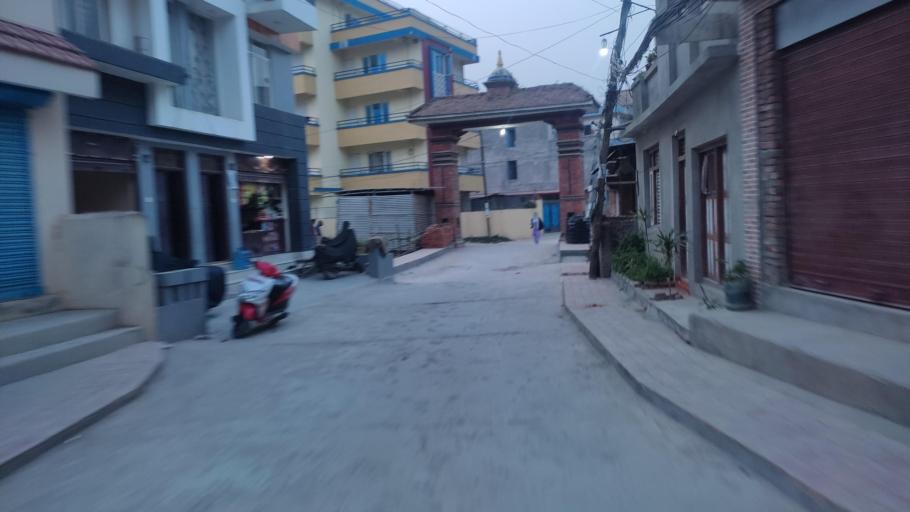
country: NP
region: Central Region
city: Kirtipur
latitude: 27.6705
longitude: 85.2763
